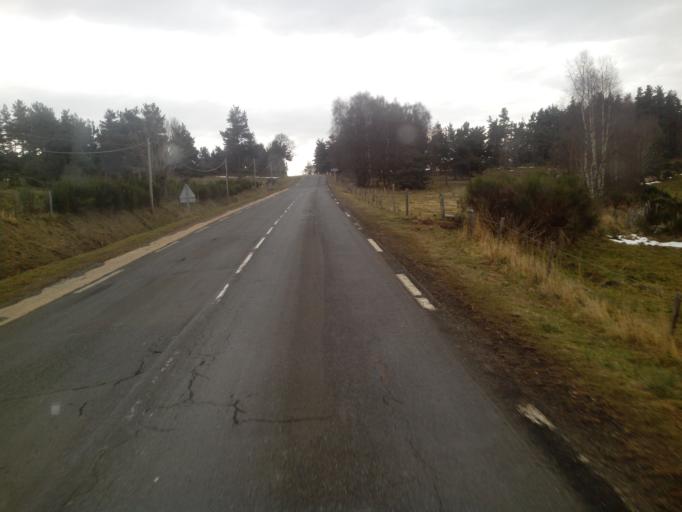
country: FR
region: Languedoc-Roussillon
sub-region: Departement de la Lozere
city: Mende
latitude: 44.6185
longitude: 3.4733
